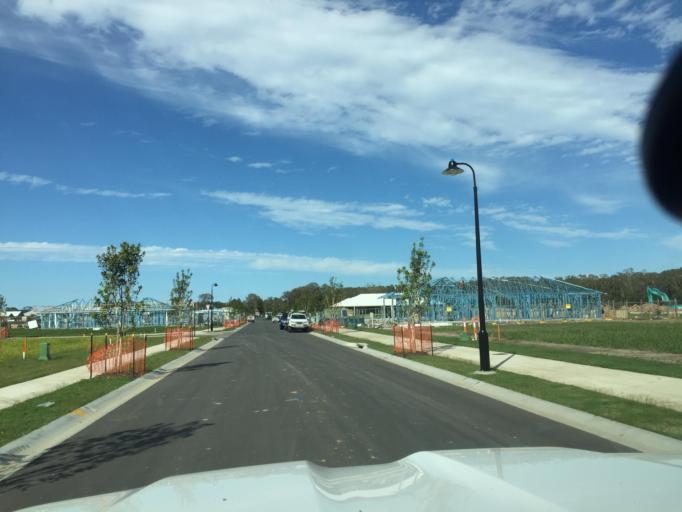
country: AU
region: Queensland
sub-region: Moreton Bay
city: Morayfield
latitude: -27.1253
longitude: 152.9966
